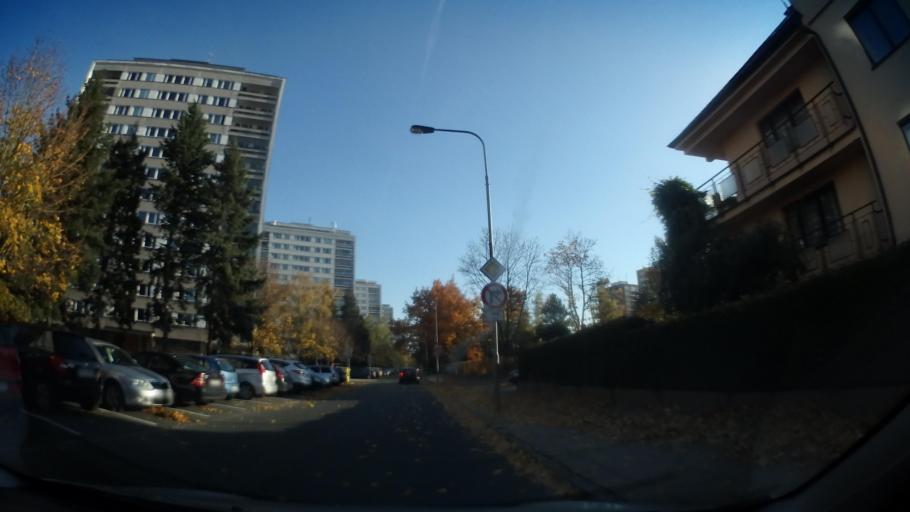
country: CZ
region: Kralovehradecky
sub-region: Okres Hradec Kralove
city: Hradec Kralove
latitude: 50.2064
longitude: 15.8179
